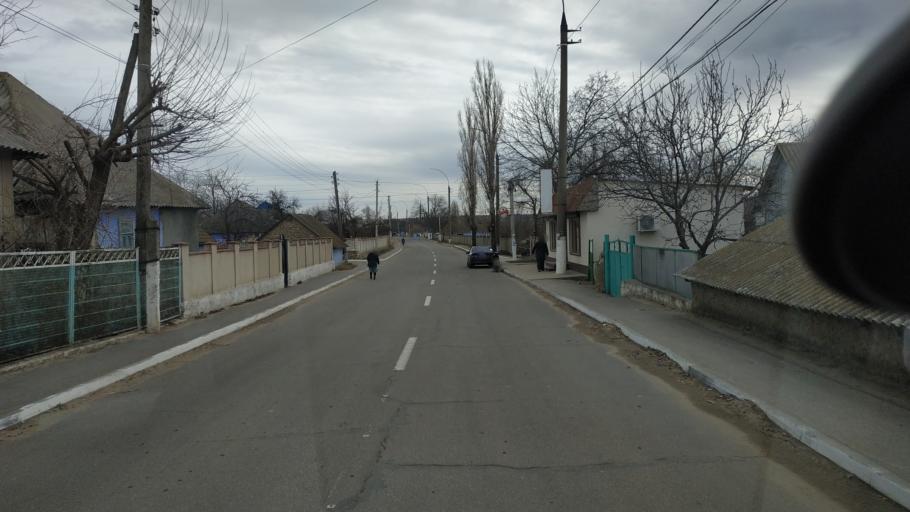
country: MD
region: Telenesti
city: Cocieri
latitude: 47.3443
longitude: 29.1139
